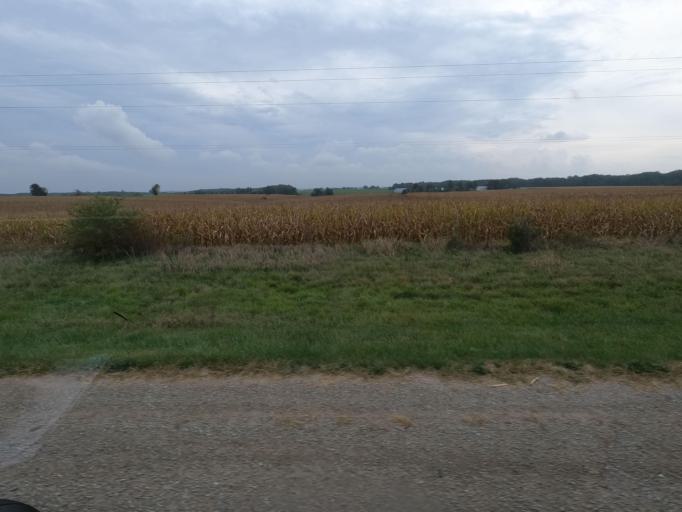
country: US
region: Iowa
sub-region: Van Buren County
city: Keosauqua
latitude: 40.8437
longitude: -92.0217
